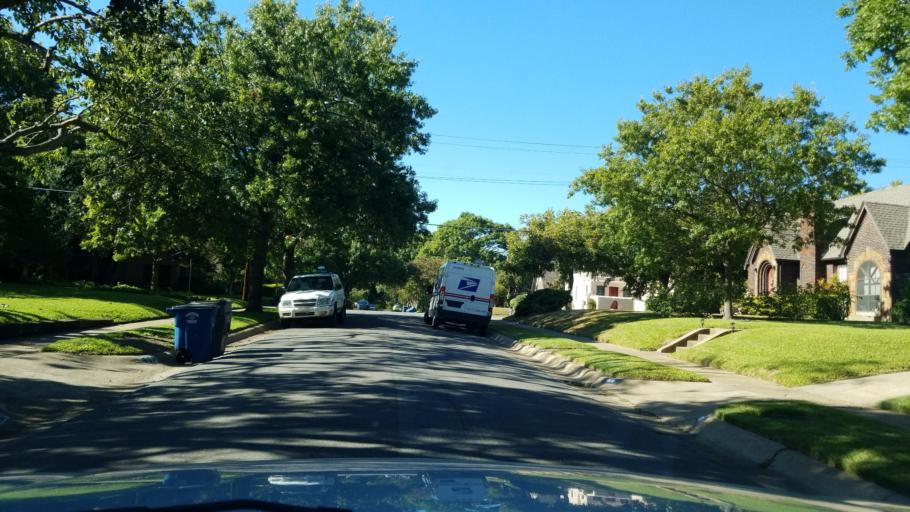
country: US
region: Texas
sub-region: Dallas County
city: Highland Park
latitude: 32.8031
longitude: -96.7427
